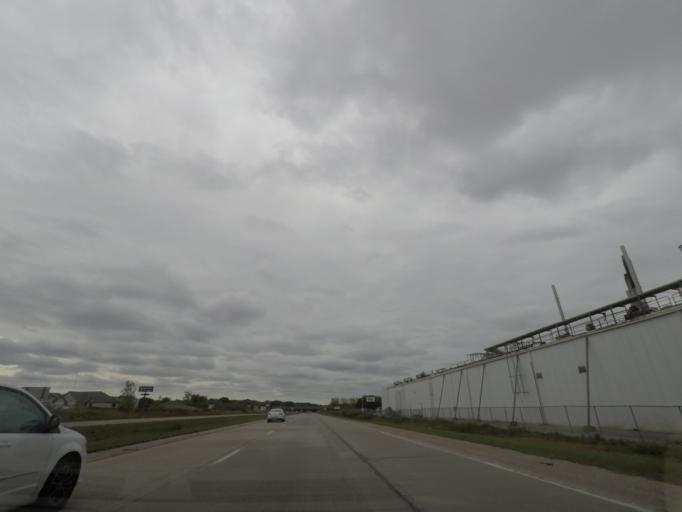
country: US
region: Iowa
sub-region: Story County
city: Nevada
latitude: 42.0075
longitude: -93.4385
